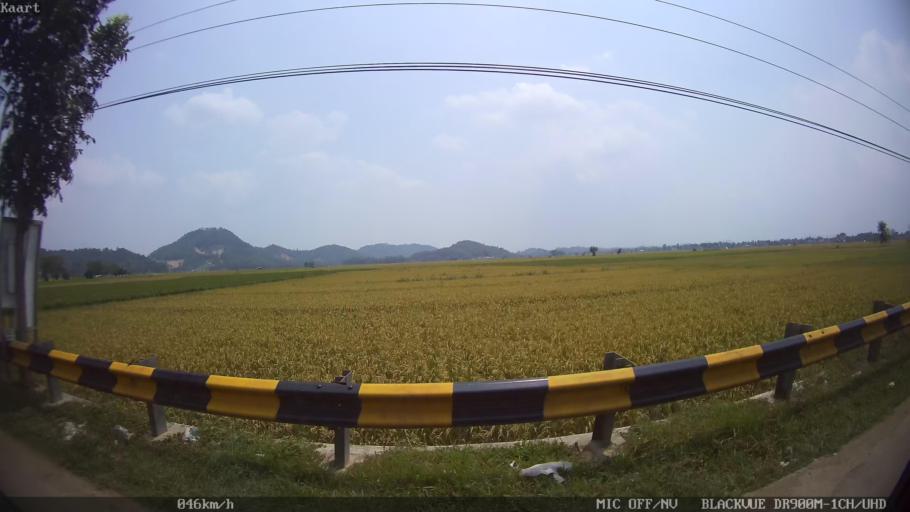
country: ID
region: Lampung
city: Pringsewu
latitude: -5.3694
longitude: 105.0102
